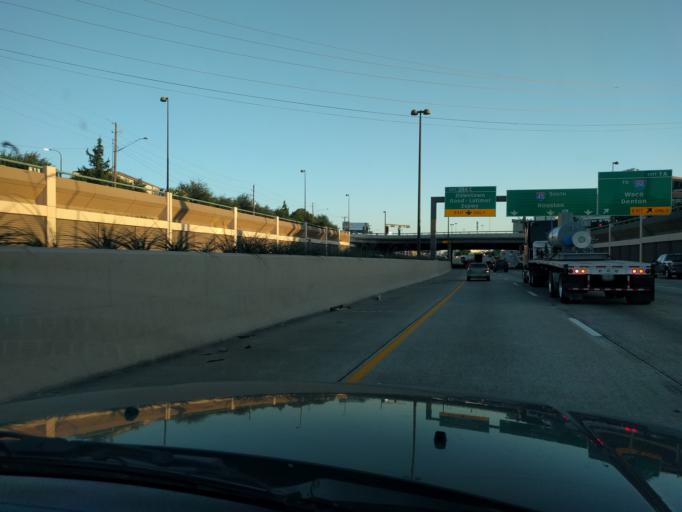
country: US
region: Texas
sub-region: Dallas County
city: Dallas
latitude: 32.8003
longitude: -96.7932
